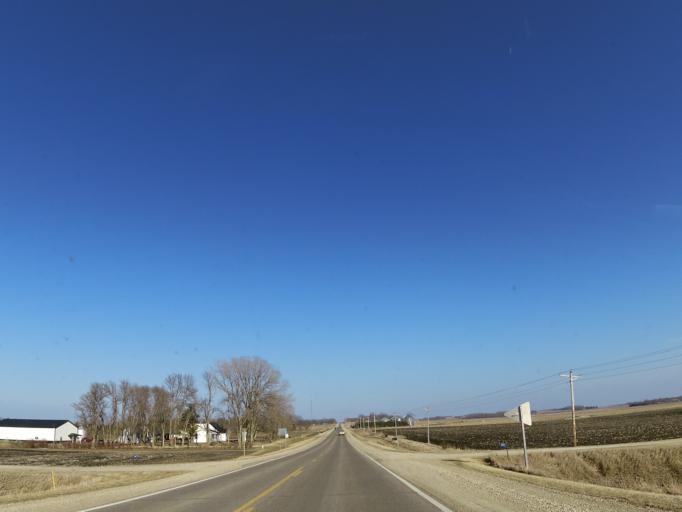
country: US
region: Iowa
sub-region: Worth County
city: Northwood
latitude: 43.4443
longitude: -93.3452
